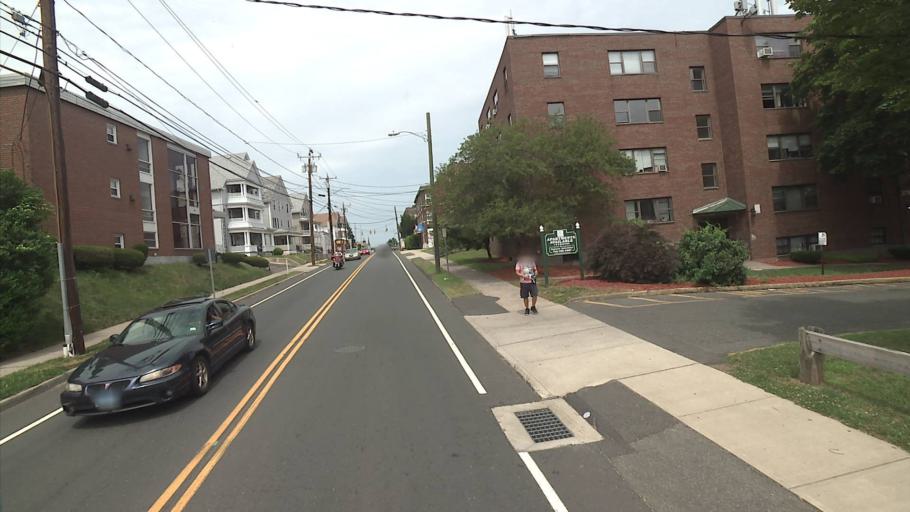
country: US
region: Connecticut
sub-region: Hartford County
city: New Britain
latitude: 41.6543
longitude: -72.7758
